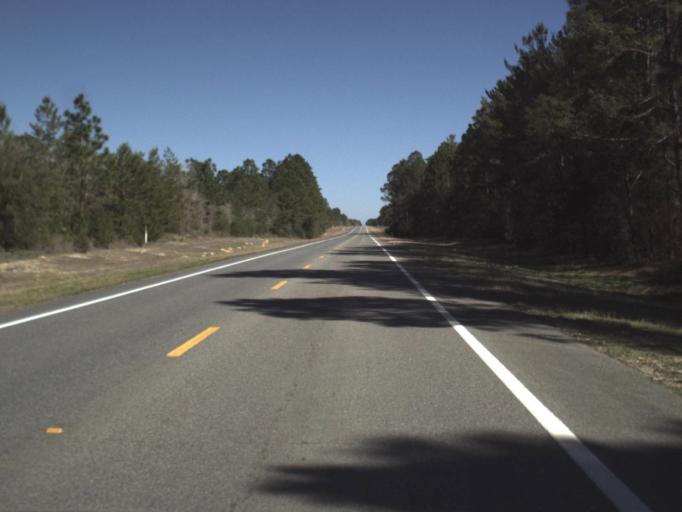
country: US
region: Florida
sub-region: Bay County
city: Youngstown
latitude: 30.4363
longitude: -85.4830
